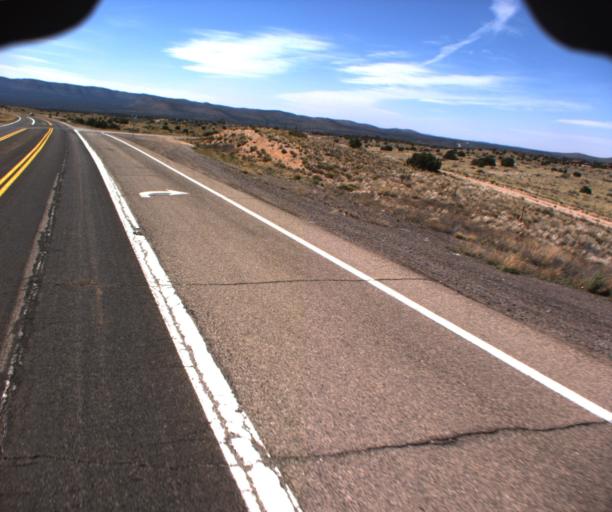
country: US
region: Arizona
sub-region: Mohave County
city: Peach Springs
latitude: 35.5239
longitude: -113.4714
